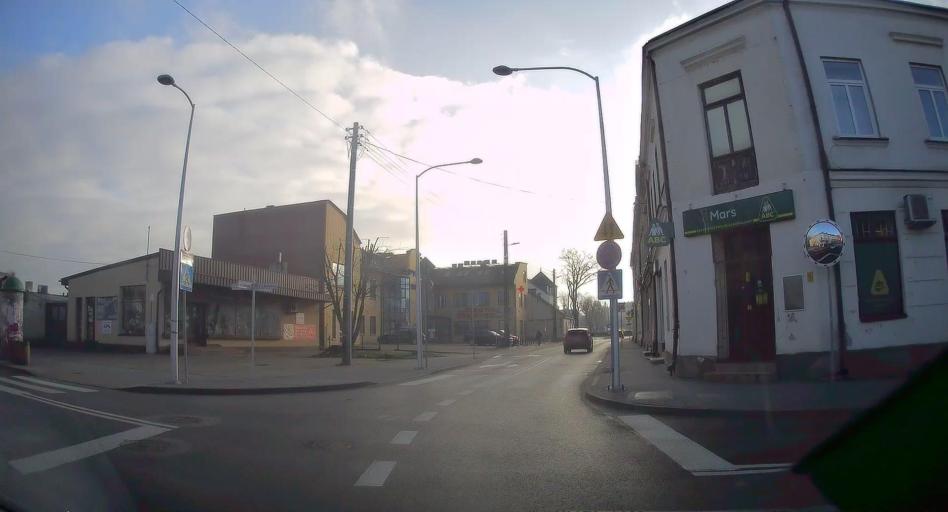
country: PL
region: Lodz Voivodeship
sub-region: Powiat rawski
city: Rawa Mazowiecka
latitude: 51.7646
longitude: 20.2547
